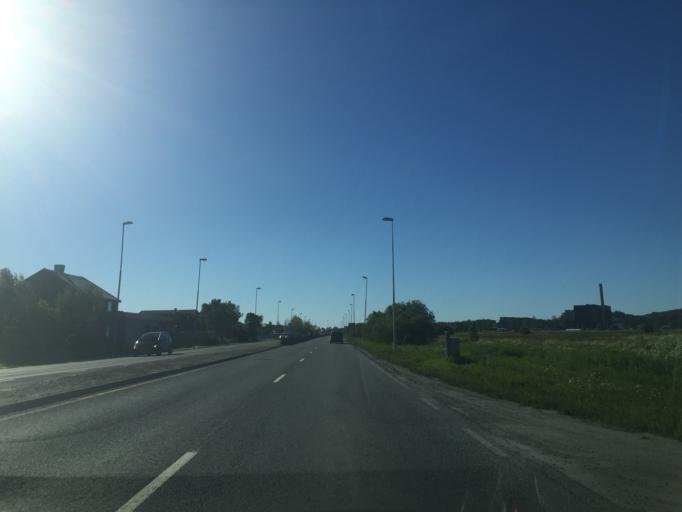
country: NO
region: Nordland
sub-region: Bodo
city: Bodo
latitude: 67.2785
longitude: 14.4317
